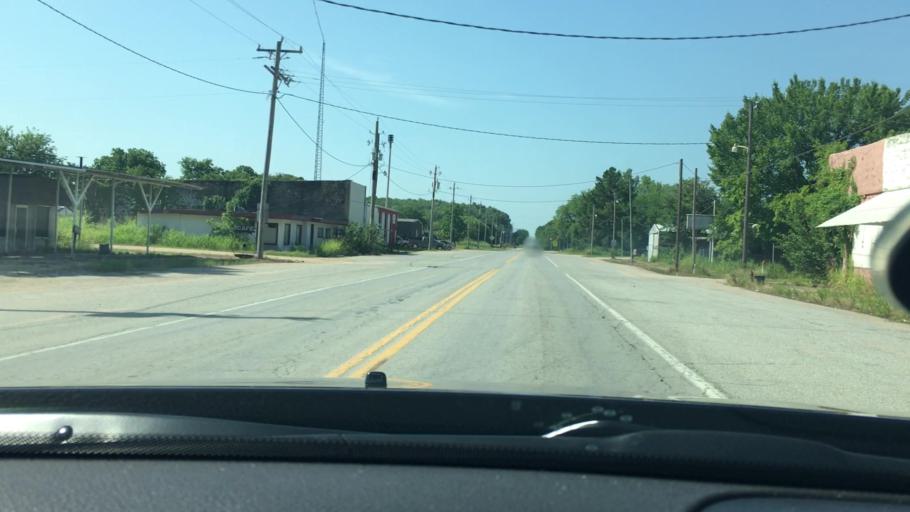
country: US
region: Oklahoma
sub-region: Coal County
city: Coalgate
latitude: 34.3745
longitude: -96.4245
